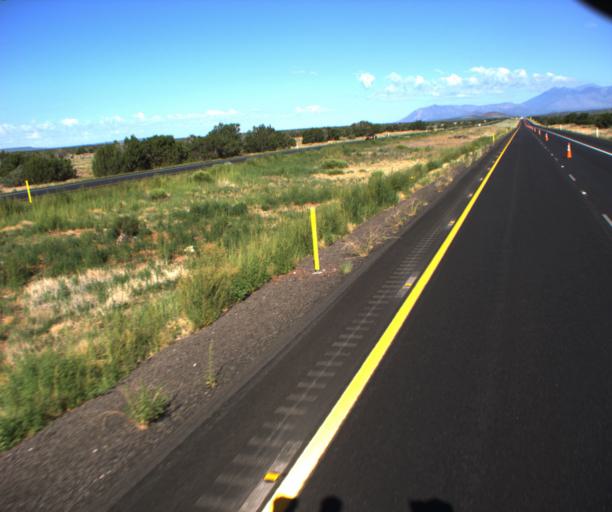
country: US
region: Arizona
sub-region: Coconino County
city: Flagstaff
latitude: 35.1675
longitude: -111.3209
